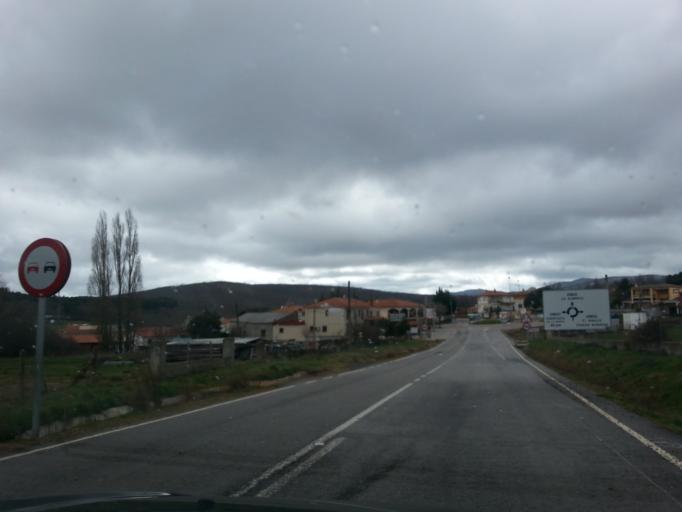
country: ES
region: Castille and Leon
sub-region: Provincia de Salamanca
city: Nava de Francia
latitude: 40.5675
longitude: -6.1286
